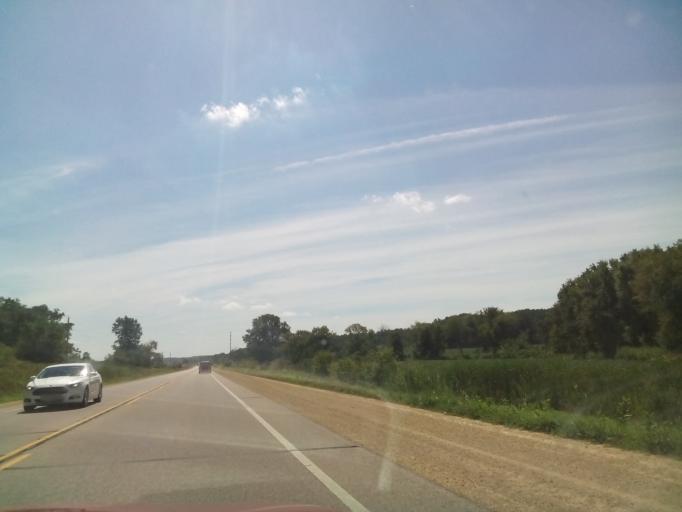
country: US
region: Wisconsin
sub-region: Green County
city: Monticello
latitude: 42.7690
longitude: -89.6250
